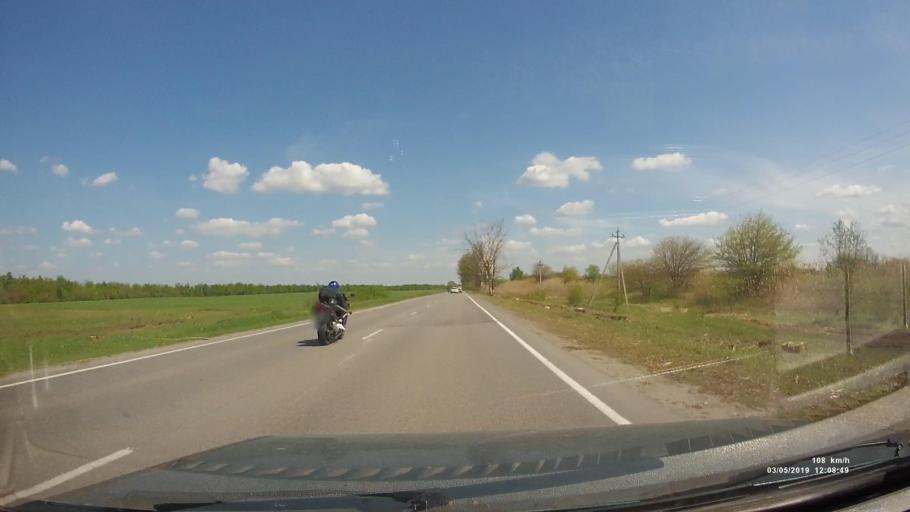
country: RU
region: Rostov
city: Bagayevskaya
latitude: 47.2900
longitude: 40.5035
